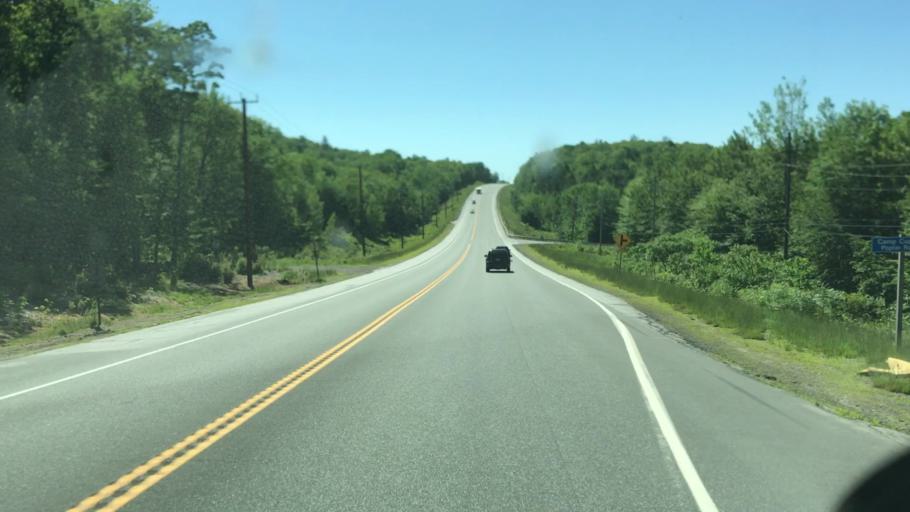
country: US
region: Maine
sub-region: Hancock County
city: Dedham
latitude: 44.6957
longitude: -68.5933
